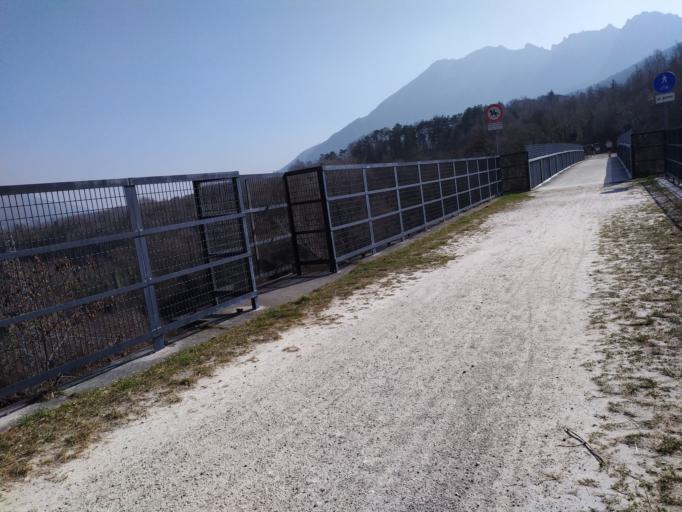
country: IT
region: Veneto
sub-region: Provincia di Vicenza
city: Arsiero
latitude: 45.7983
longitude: 11.3588
